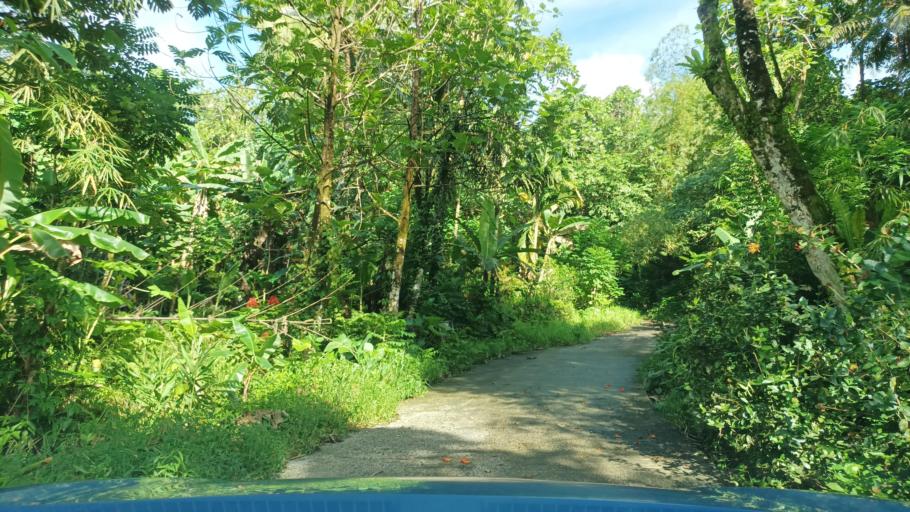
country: FM
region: Pohnpei
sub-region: Kolonia Municipality
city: Kolonia Town
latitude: 6.9623
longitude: 158.1850
